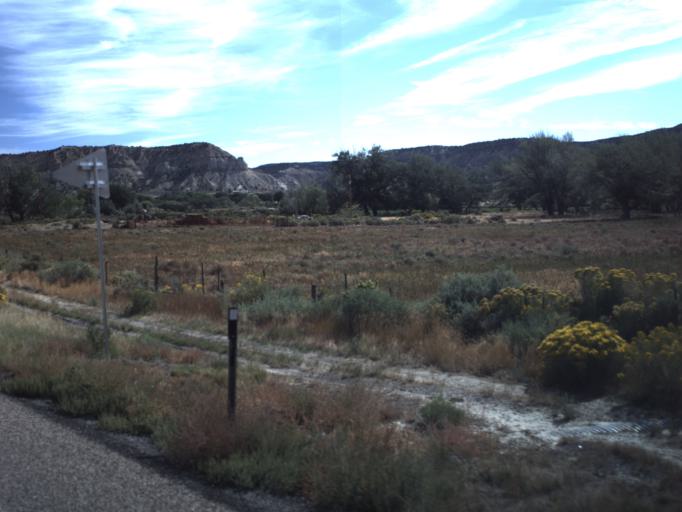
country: US
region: Utah
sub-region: Garfield County
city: Panguitch
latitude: 37.5619
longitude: -112.0133
